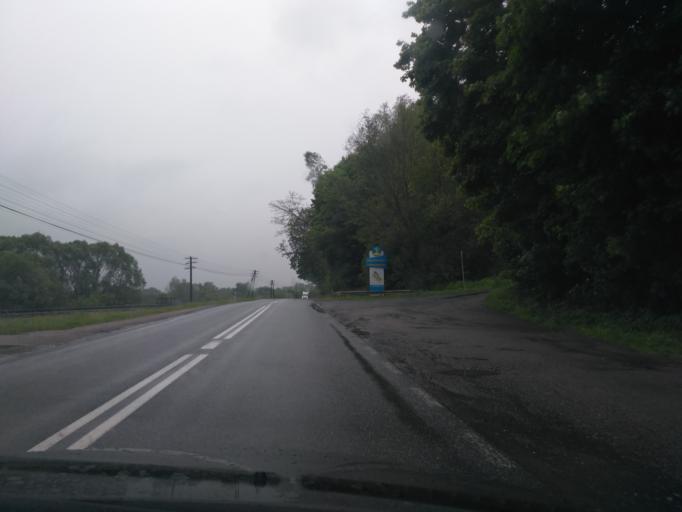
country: PL
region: Subcarpathian Voivodeship
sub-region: Powiat krosnienski
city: Leki
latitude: 49.8105
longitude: 21.6364
